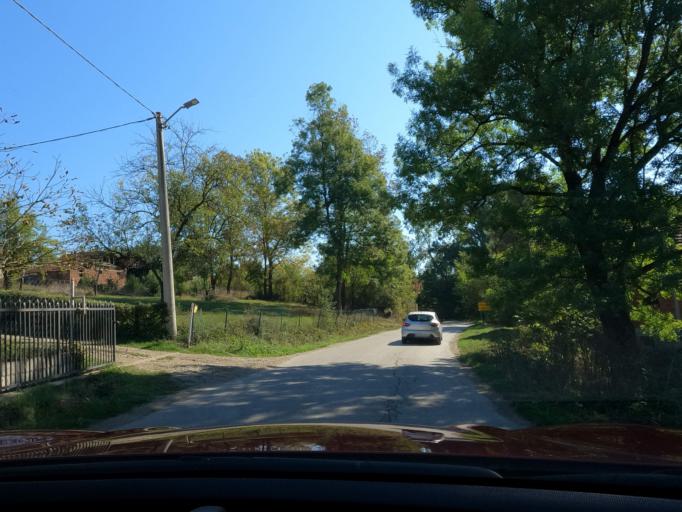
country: RS
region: Central Serbia
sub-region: Raski Okrug
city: Kraljevo
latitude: 43.7717
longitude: 20.6584
